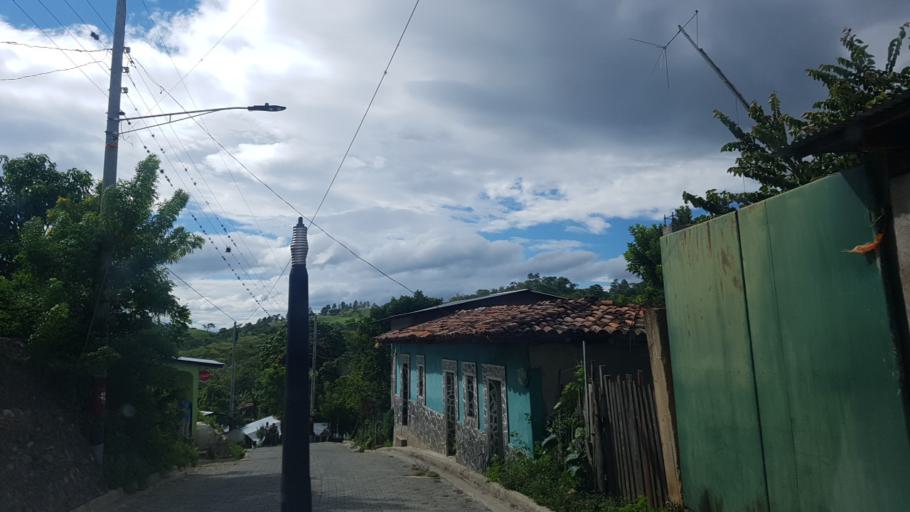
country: HN
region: El Paraiso
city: Oropoli
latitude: 13.7465
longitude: -86.7080
